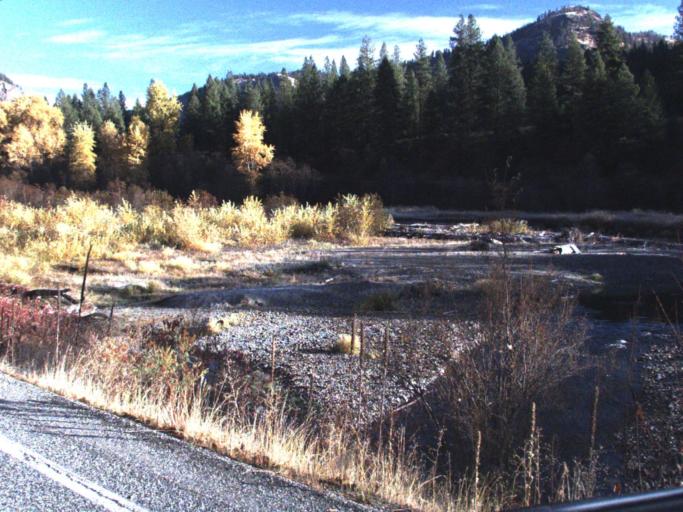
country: US
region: Washington
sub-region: Ferry County
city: Republic
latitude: 48.3841
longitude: -118.7484
